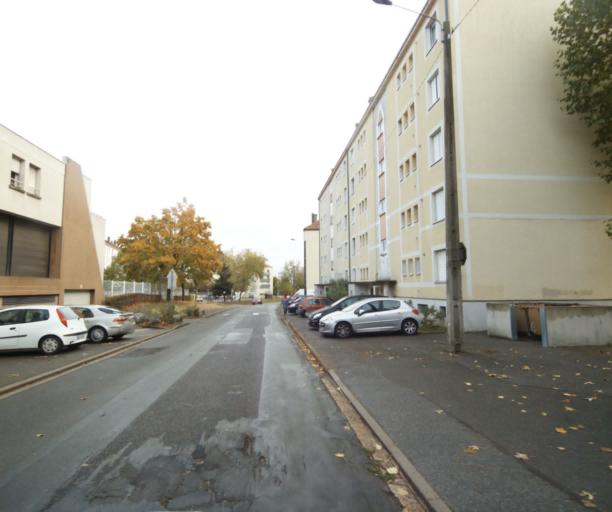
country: FR
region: Centre
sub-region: Departement d'Eure-et-Loir
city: Dreux
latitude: 48.7315
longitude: 1.3800
